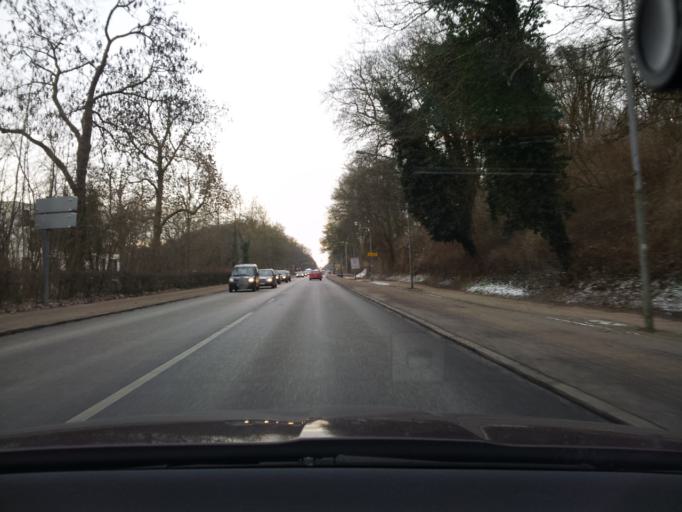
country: DE
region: Schleswig-Holstein
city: Luebeck
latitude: 53.8638
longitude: 10.6783
